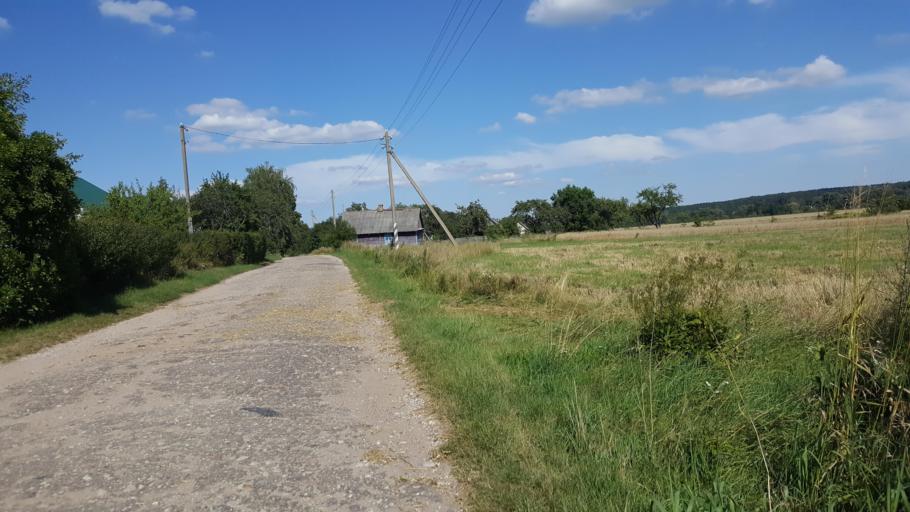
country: BY
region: Brest
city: Charnawchytsy
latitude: 52.3270
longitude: 23.6378
